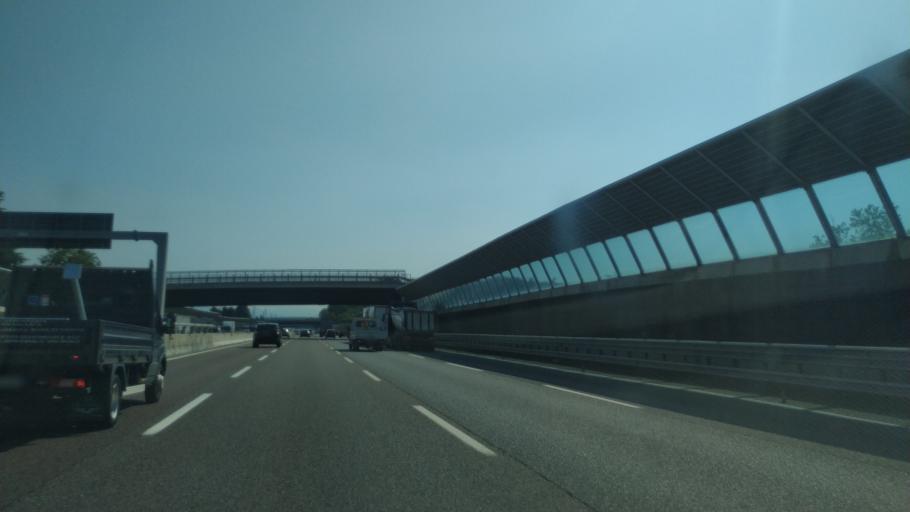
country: IT
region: Lombardy
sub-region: Citta metropolitana di Milano
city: Trezzo sull'Adda
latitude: 45.6008
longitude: 9.5152
